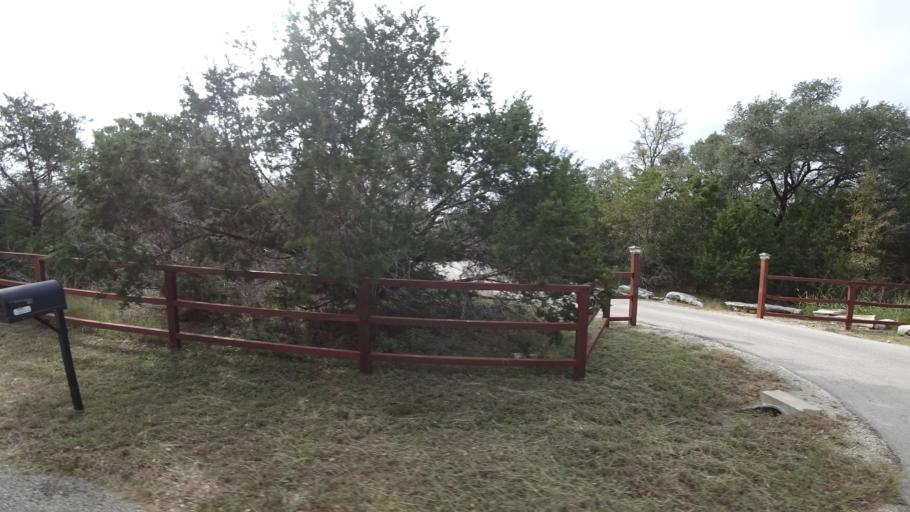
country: US
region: Texas
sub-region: Travis County
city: Shady Hollow
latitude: 30.1481
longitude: -97.8904
